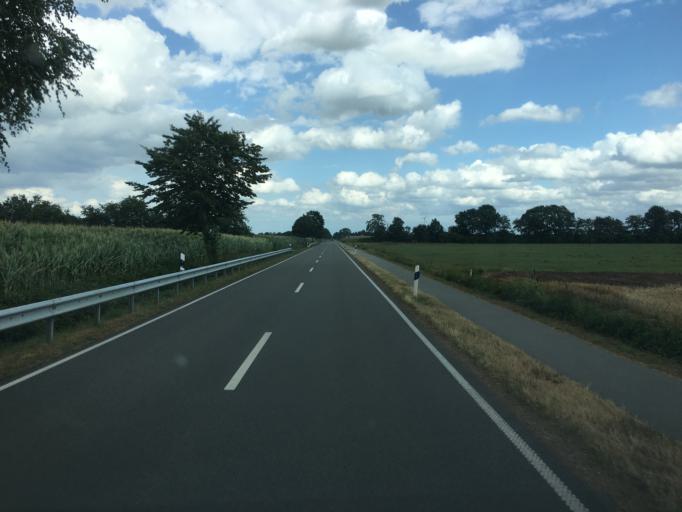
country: DE
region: Lower Saxony
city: Barssel
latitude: 53.0766
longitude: 7.7428
